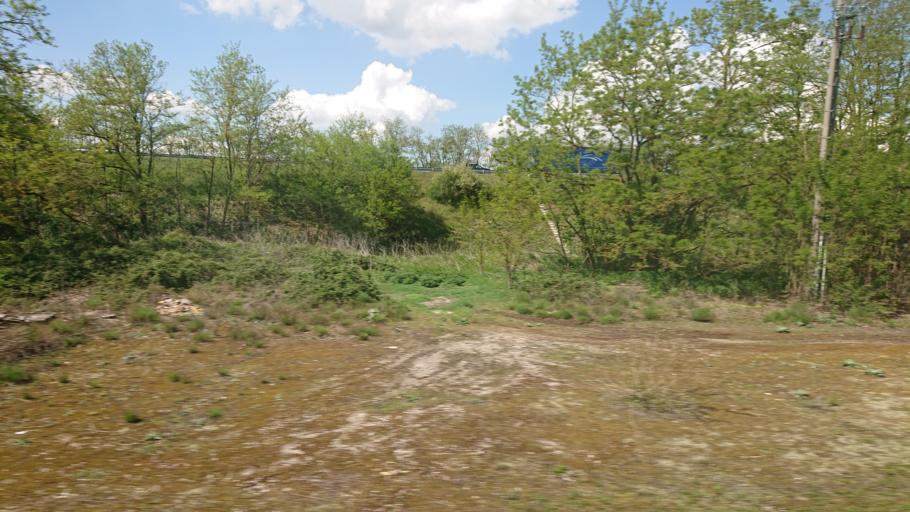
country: FR
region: Rhone-Alpes
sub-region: Departement de l'Ain
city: Leyment
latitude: 45.9351
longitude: 5.2811
